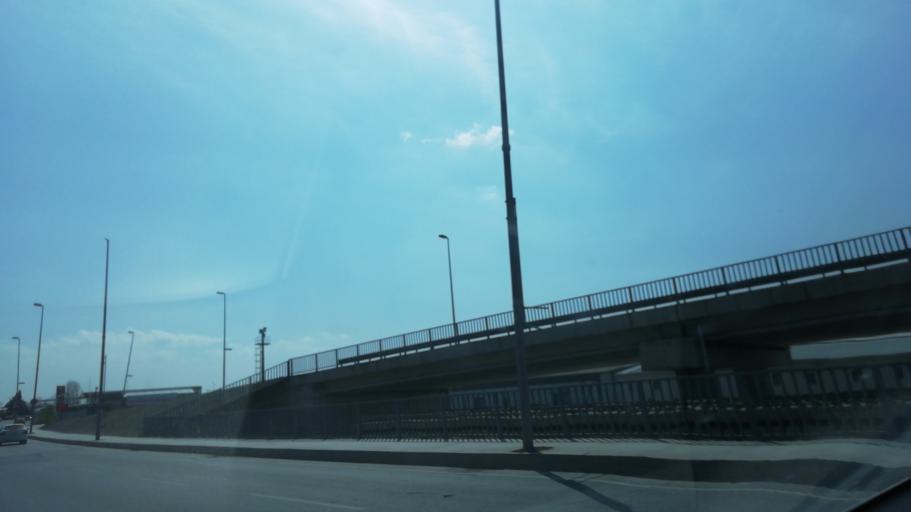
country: TR
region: Istanbul
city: Mahmutbey
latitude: 41.0165
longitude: 28.7684
